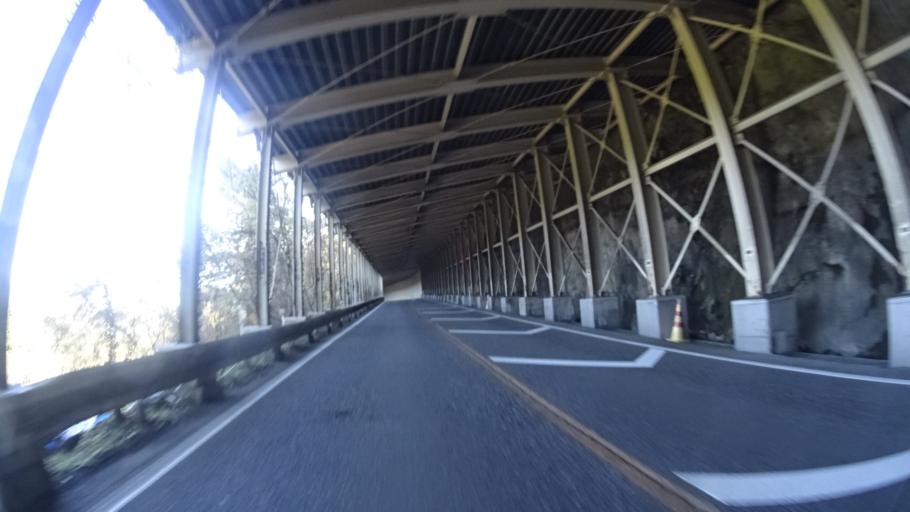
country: JP
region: Ishikawa
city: Tsurugi-asahimachi
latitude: 36.3684
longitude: 136.6122
